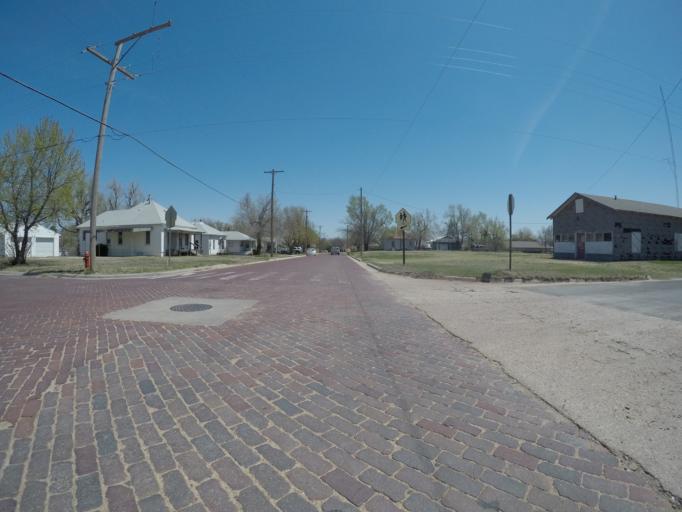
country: US
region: Kansas
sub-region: Pratt County
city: Pratt
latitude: 37.6421
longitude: -98.7510
